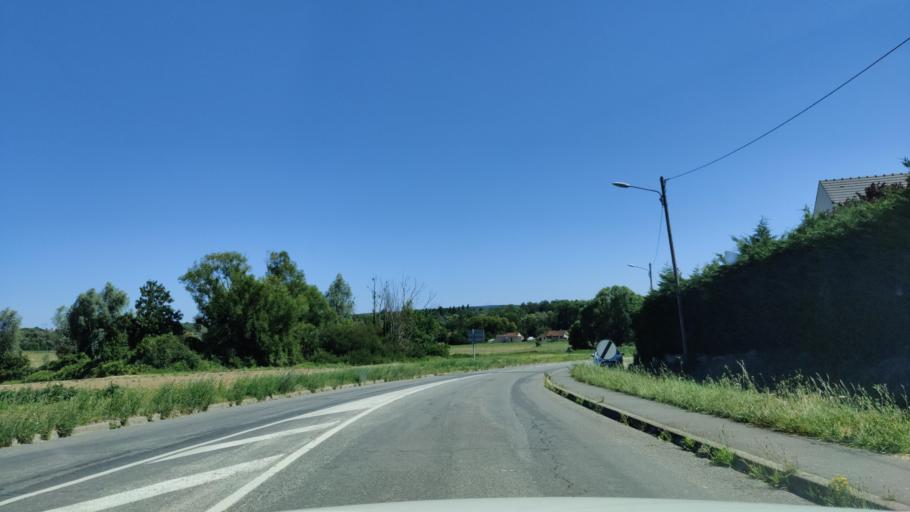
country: FR
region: Ile-de-France
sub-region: Departement de l'Essonne
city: Bruyeres-le-Chatel
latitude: 48.5860
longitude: 2.1916
